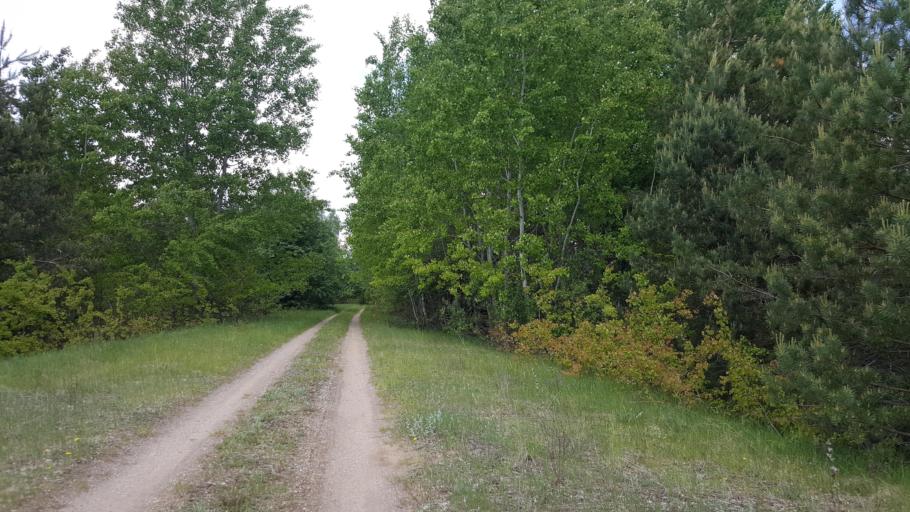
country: BY
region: Brest
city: Kamyanyets
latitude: 52.4818
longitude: 23.9650
